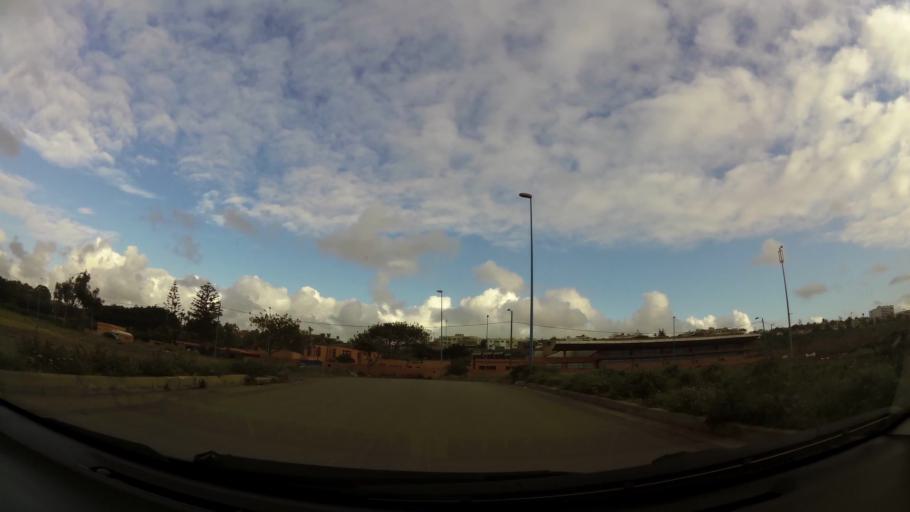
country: MA
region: Grand Casablanca
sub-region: Casablanca
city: Casablanca
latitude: 33.5778
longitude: -7.6906
